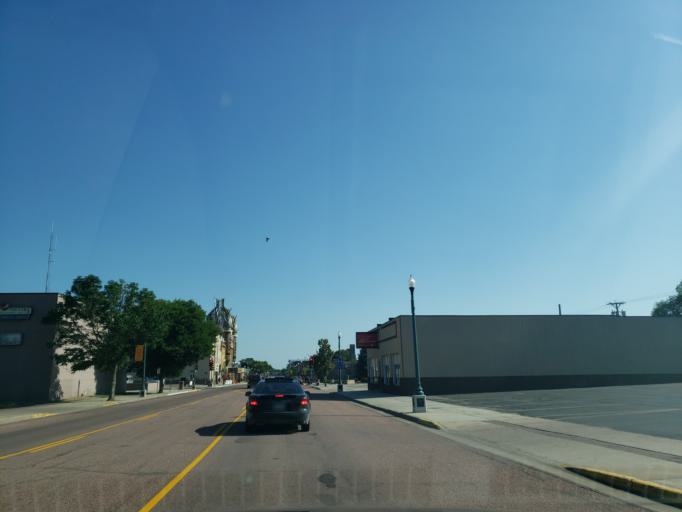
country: US
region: South Dakota
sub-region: Davison County
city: Mitchell
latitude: 43.7164
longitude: -98.0256
